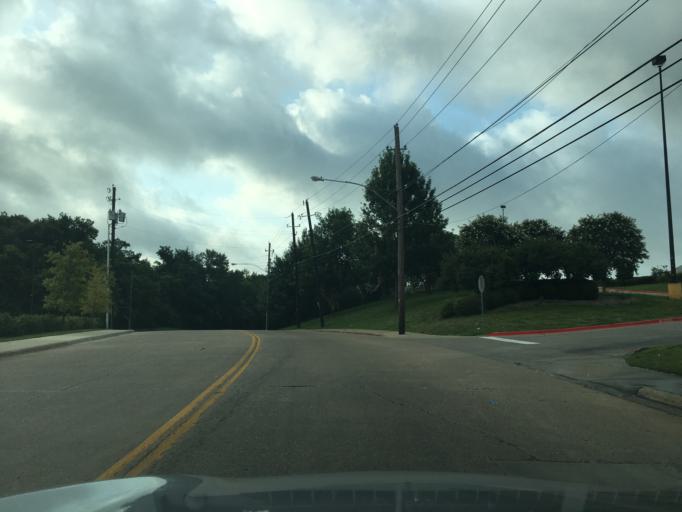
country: US
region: Texas
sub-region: Dallas County
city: Highland Park
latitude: 32.8624
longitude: -96.7487
